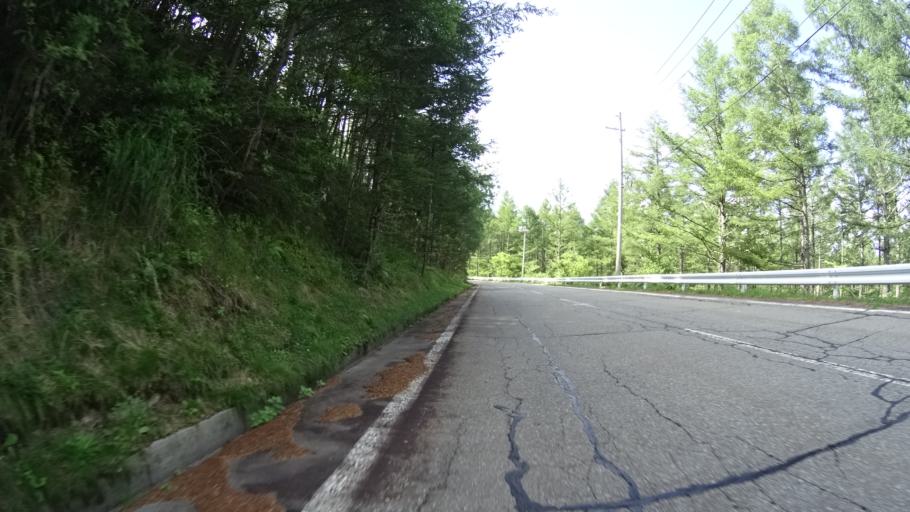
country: JP
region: Nagano
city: Saku
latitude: 36.0590
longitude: 138.3949
